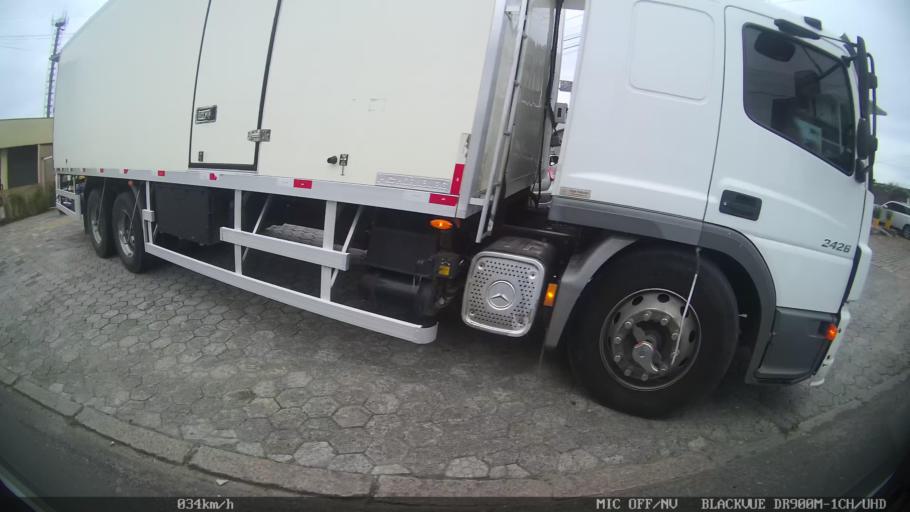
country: BR
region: Santa Catarina
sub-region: Joinville
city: Joinville
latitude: -26.2740
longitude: -48.8319
